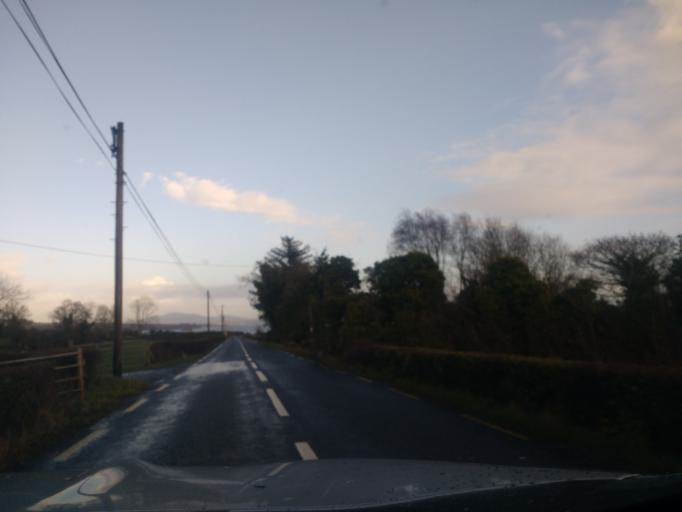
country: IE
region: Ulster
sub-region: County Donegal
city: Ramelton
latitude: 55.0638
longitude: -7.6121
